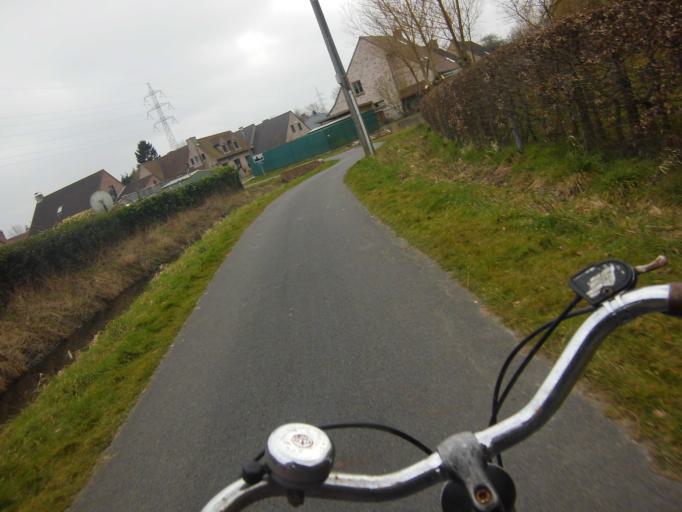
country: BE
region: Flanders
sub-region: Provincie West-Vlaanderen
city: Brugge
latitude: 51.2360
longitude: 3.2082
